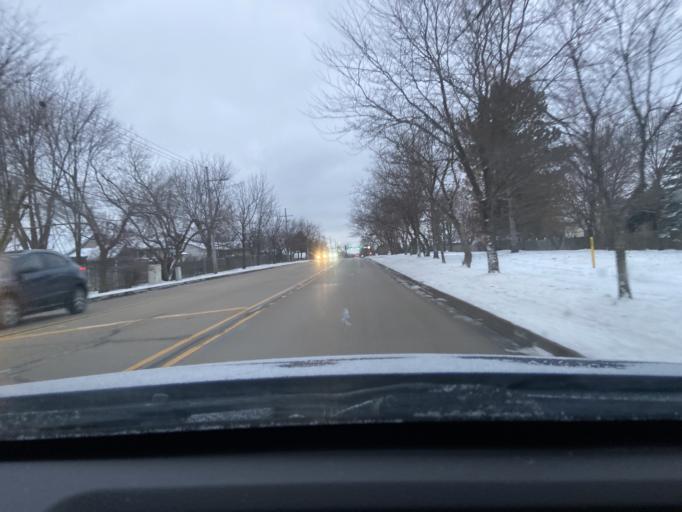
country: US
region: Illinois
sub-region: Lake County
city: Grayslake
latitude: 42.3493
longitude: -88.0240
